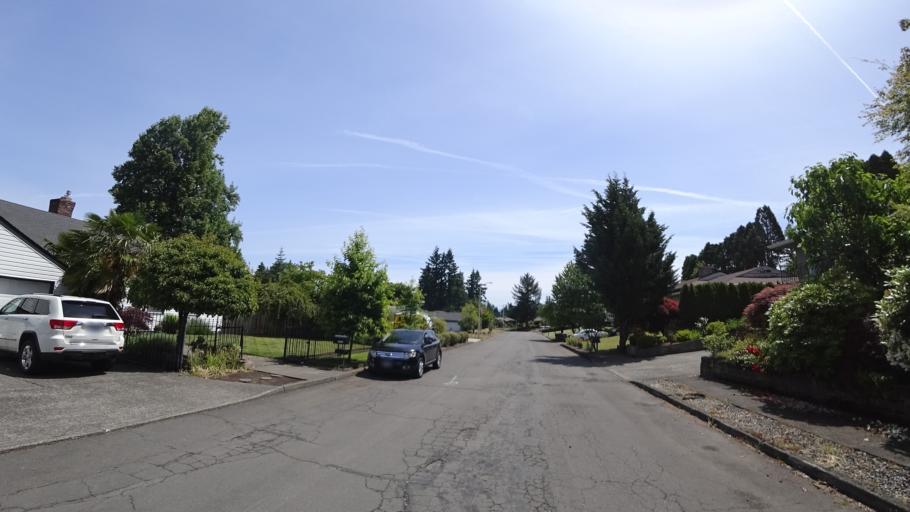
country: US
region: Oregon
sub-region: Multnomah County
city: Fairview
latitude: 45.5432
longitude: -122.4992
